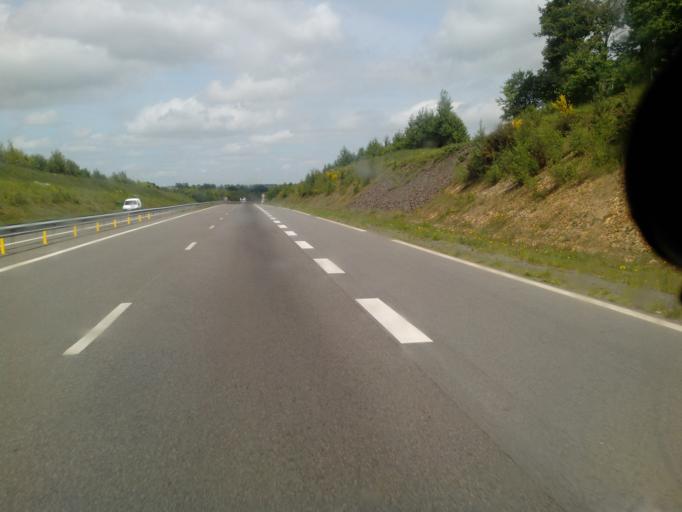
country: FR
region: Brittany
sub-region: Departement d'Ille-et-Vilaine
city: Betton
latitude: 48.1819
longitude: -1.6247
